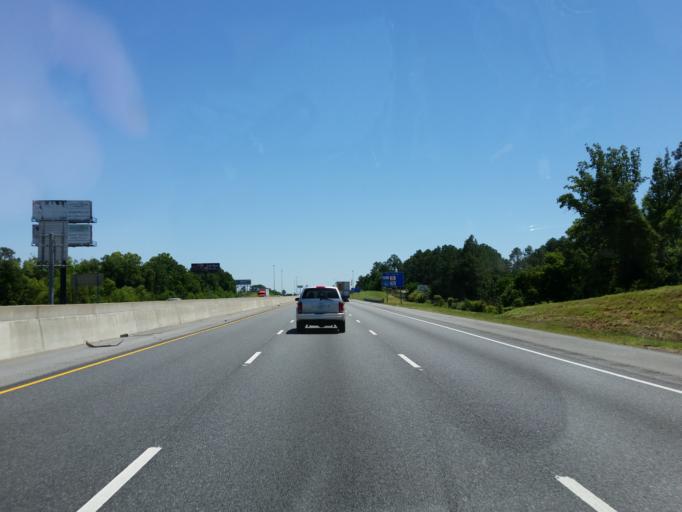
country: US
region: Georgia
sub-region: Turner County
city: Ashburn
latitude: 31.7214
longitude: -83.6415
